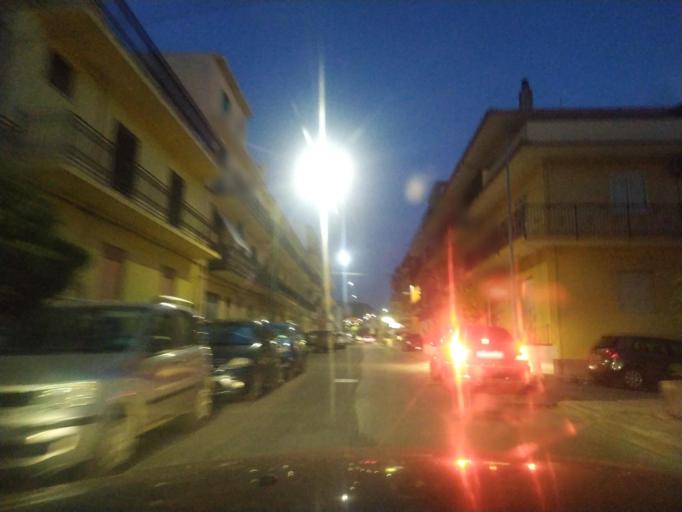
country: IT
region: Sicily
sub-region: Messina
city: Terme
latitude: 38.1388
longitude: 15.1617
